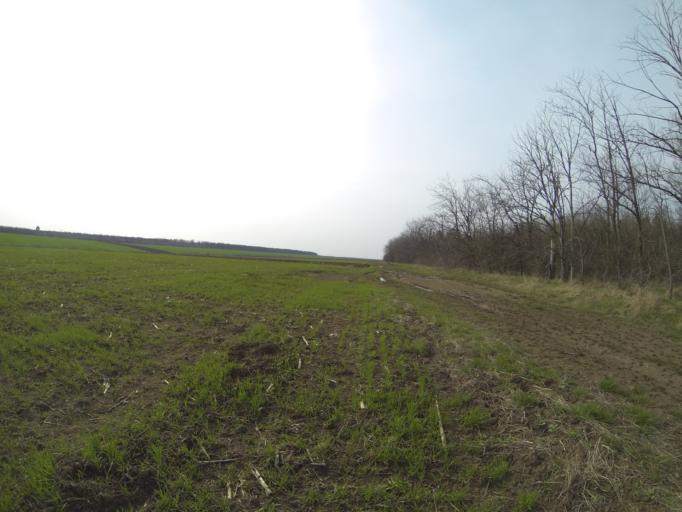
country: RO
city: Varvoru
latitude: 44.2714
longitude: 23.6647
